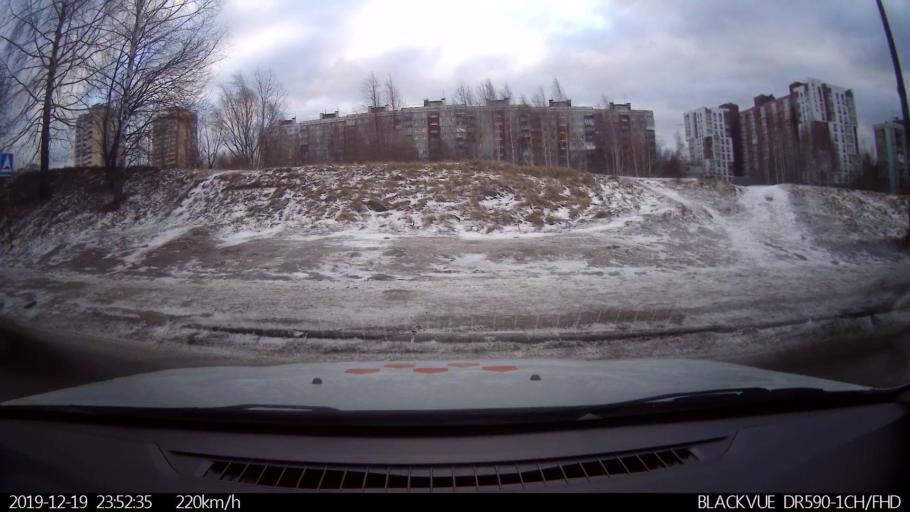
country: RU
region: Vologda
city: Molochnoye
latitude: 58.9846
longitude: 39.4893
